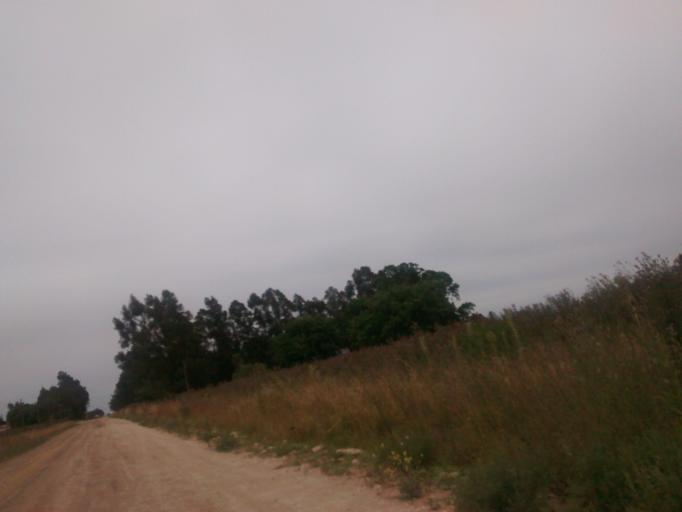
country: AR
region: Buenos Aires
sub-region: Partido de Loberia
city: Loberia
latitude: -38.1915
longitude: -58.7375
